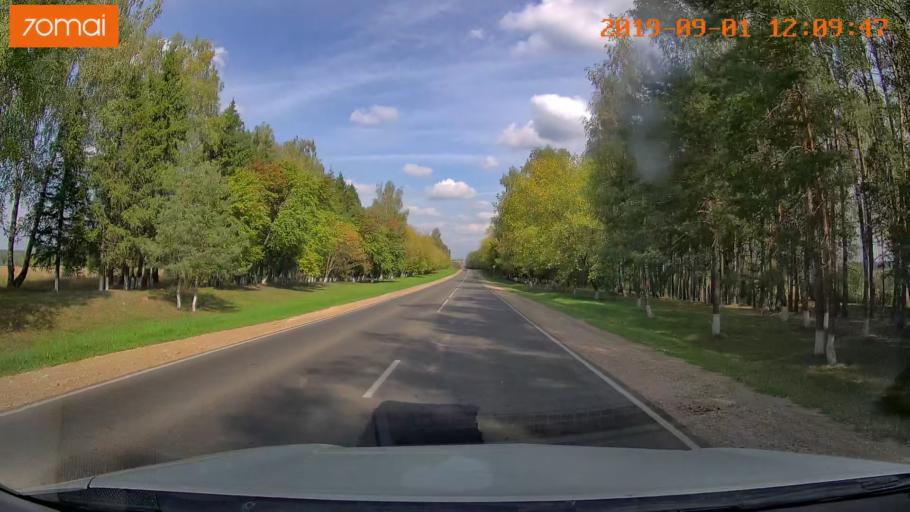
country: RU
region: Kaluga
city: Maloyaroslavets
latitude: 54.9842
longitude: 36.4283
